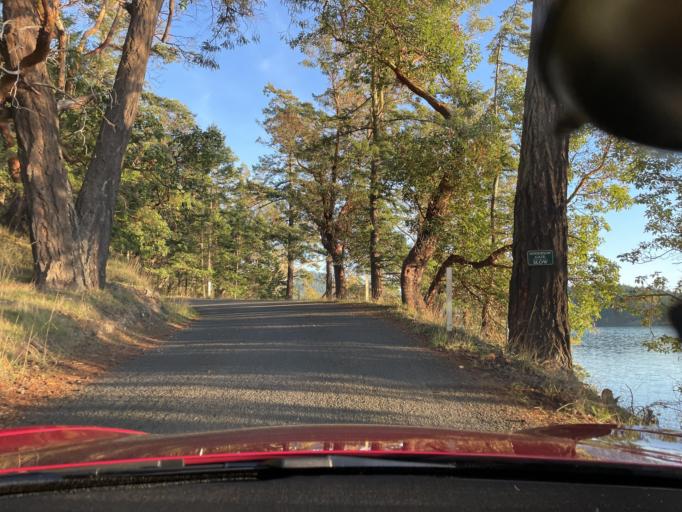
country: US
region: Washington
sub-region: San Juan County
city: Friday Harbor
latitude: 48.6000
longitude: -123.1572
